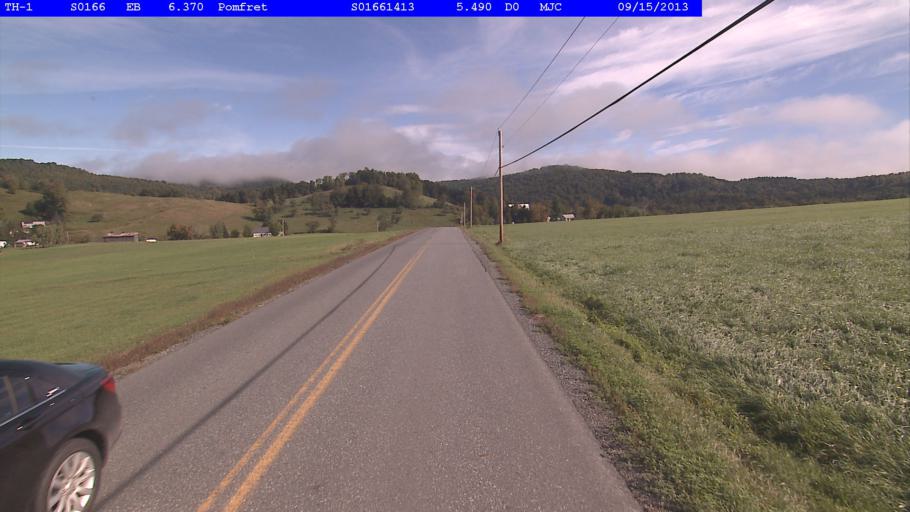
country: US
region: Vermont
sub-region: Windsor County
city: Woodstock
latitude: 43.7192
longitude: -72.5034
